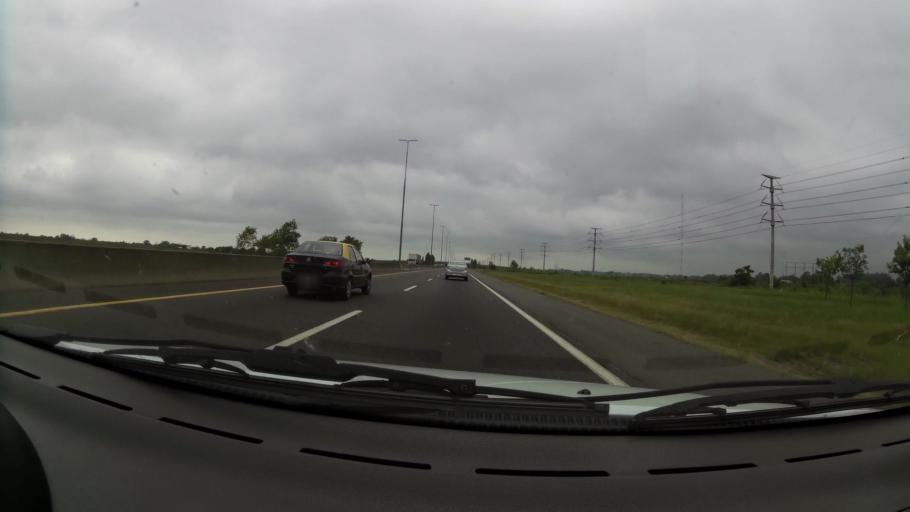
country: AR
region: Buenos Aires
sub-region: Partido de La Plata
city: La Plata
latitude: -34.8353
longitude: -58.0773
